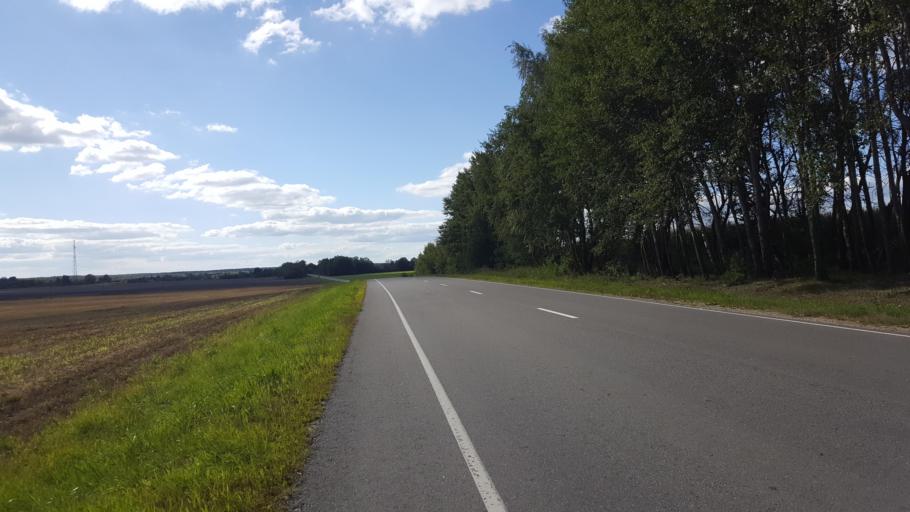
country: BY
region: Brest
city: Zhabinka
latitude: 52.3566
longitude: 24.1721
